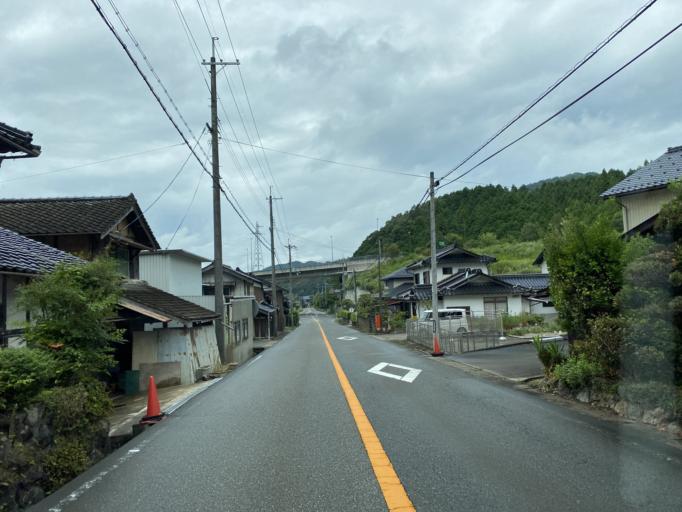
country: JP
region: Kyoto
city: Fukuchiyama
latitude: 35.3030
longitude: 134.9148
